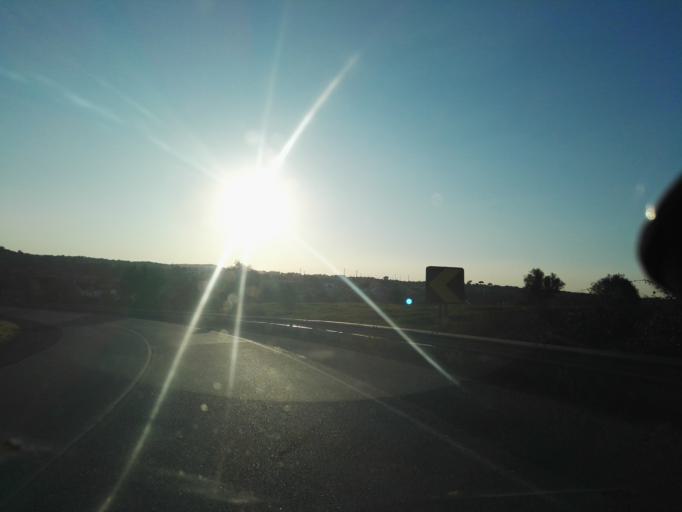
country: PT
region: Evora
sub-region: Montemor-O-Novo
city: Montemor-o-Novo
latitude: 38.6495
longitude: -8.2330
